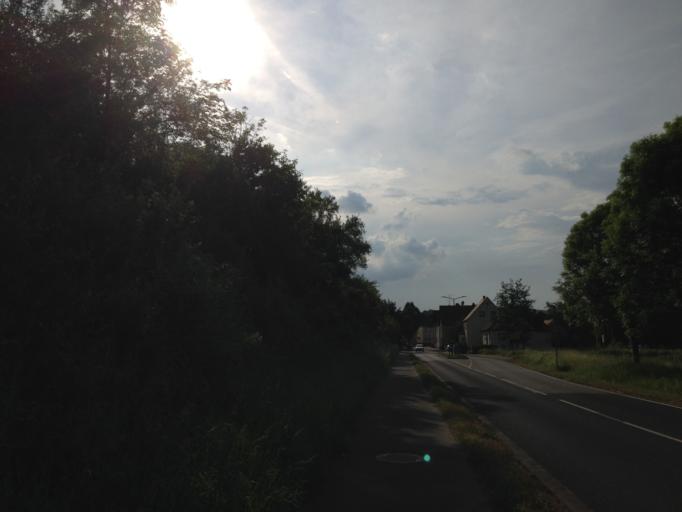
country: DE
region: Hesse
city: Allendorf an der Lahn
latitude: 50.5475
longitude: 8.6220
